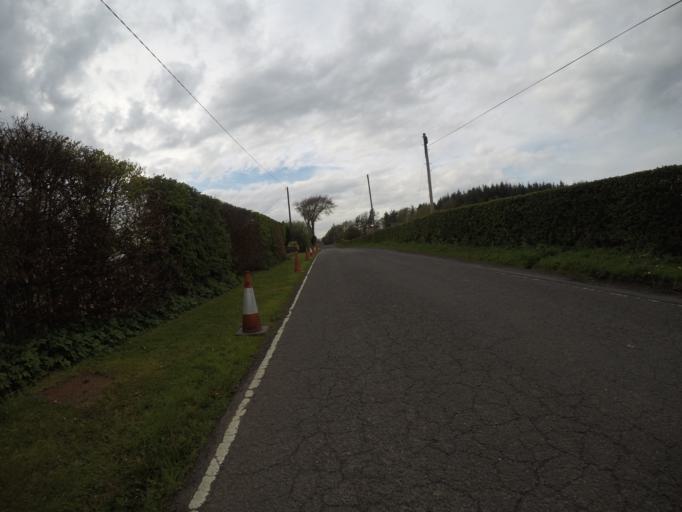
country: GB
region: Scotland
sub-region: East Ayrshire
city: Kilmarnock
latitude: 55.6404
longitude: -4.4756
